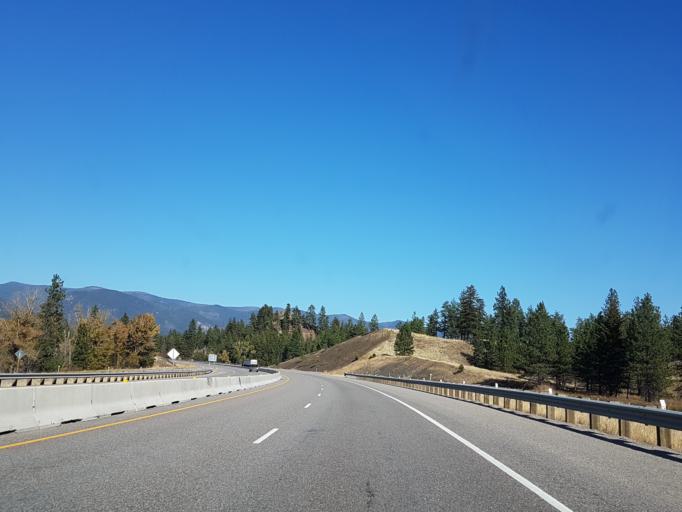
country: US
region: Montana
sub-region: Missoula County
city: Frenchtown
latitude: 47.0195
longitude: -114.3669
